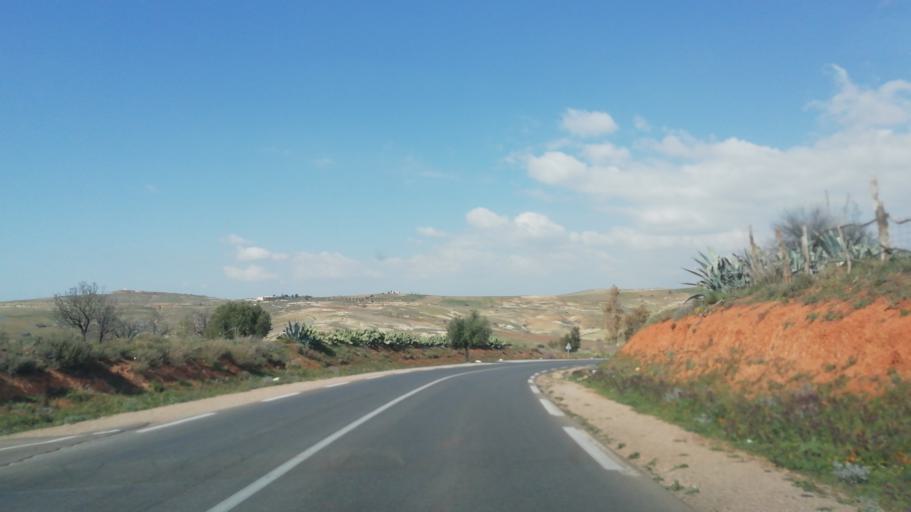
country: DZ
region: Mascara
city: Mascara
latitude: 35.5333
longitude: 0.1112
